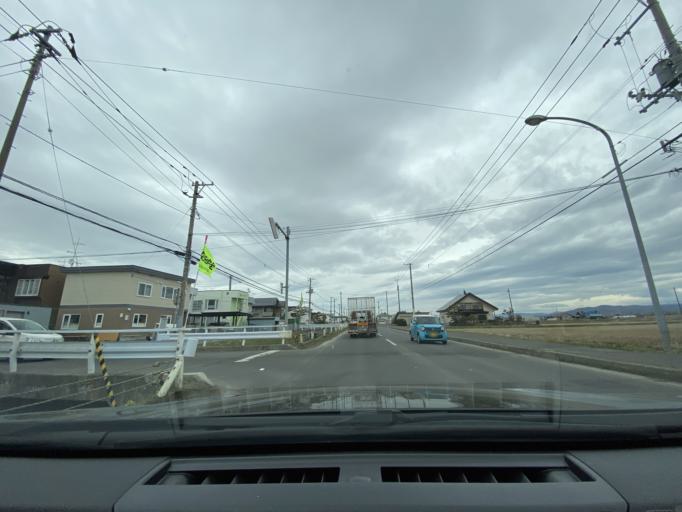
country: JP
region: Hokkaido
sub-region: Asahikawa-shi
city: Asahikawa
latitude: 43.7843
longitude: 142.4157
